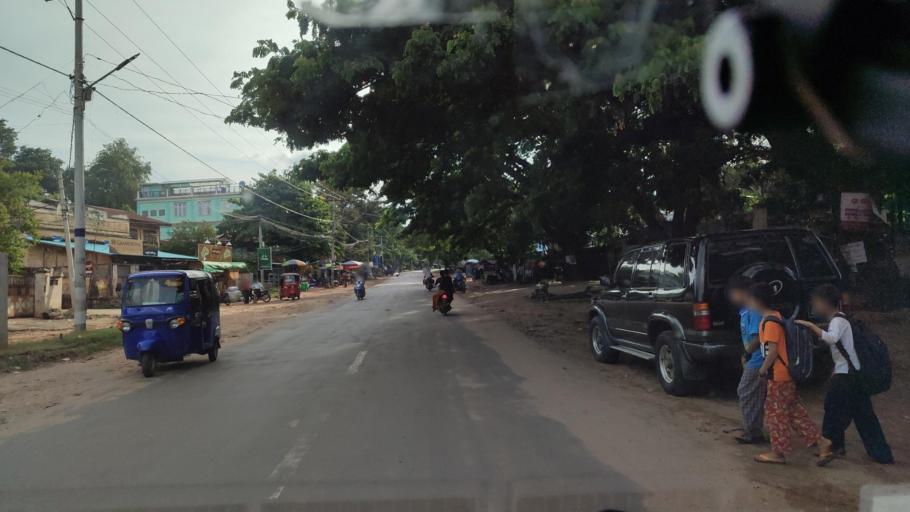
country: MM
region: Magway
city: Chauk
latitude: 20.8352
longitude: 95.1246
